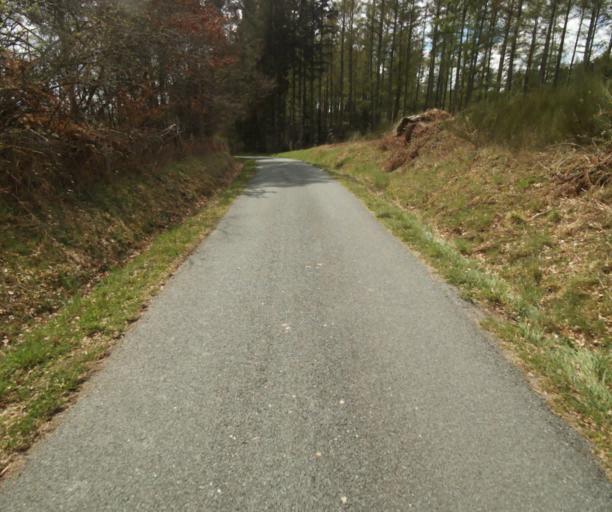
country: FR
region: Limousin
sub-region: Departement de la Correze
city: Correze
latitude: 45.3761
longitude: 1.9635
